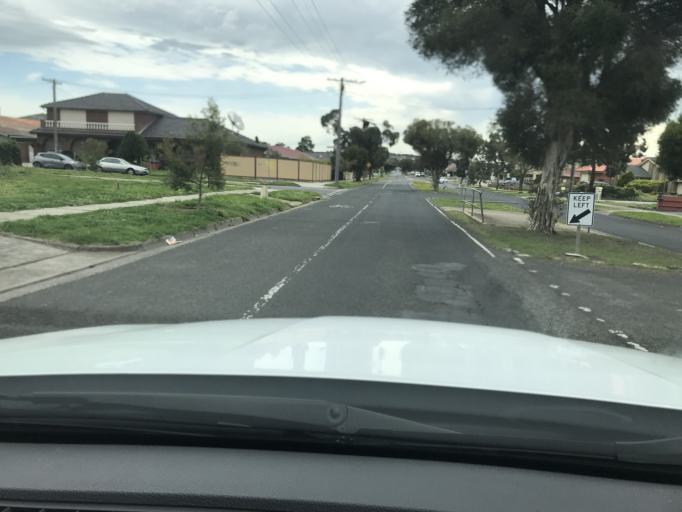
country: AU
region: Victoria
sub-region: Hume
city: Craigieburn
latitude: -37.5940
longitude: 144.9374
